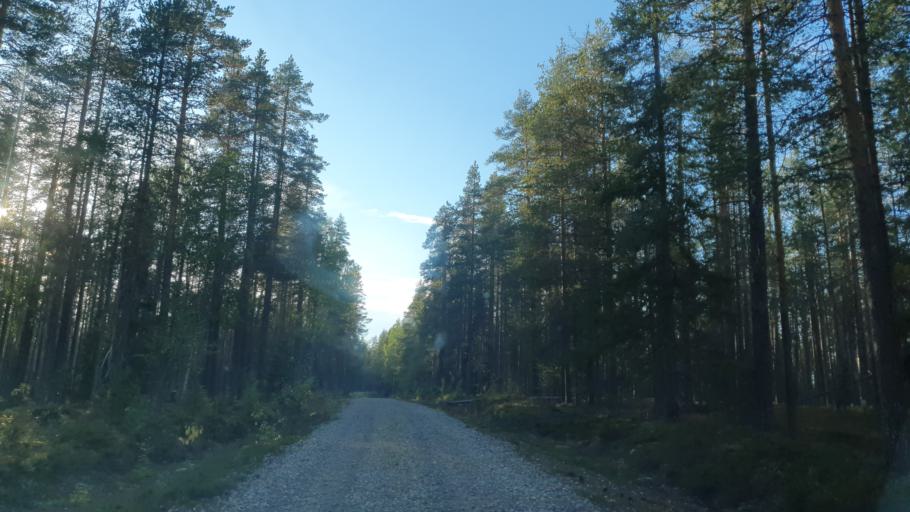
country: FI
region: Kainuu
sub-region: Kehys-Kainuu
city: Kuhmo
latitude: 64.3291
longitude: 30.0293
